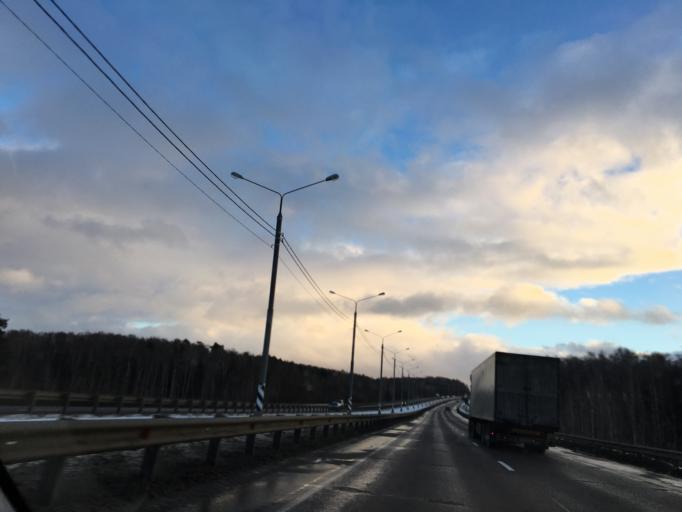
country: RU
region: Tula
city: Zaokskiy
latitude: 54.8200
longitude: 37.4744
